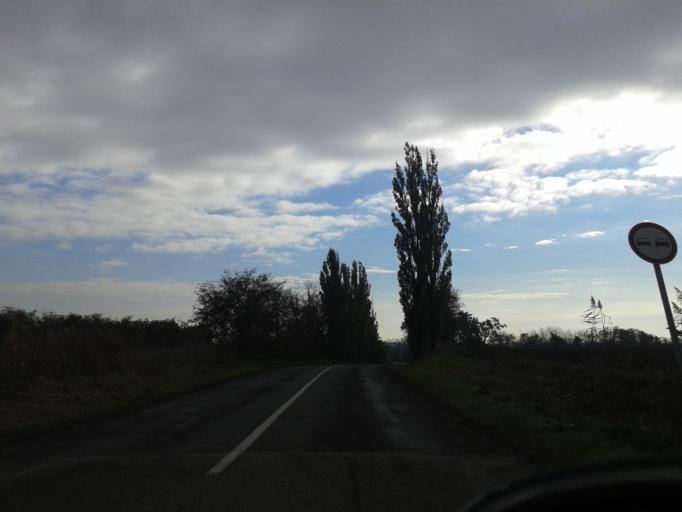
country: HU
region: Fejer
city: Ivancsa
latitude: 47.1272
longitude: 18.8263
